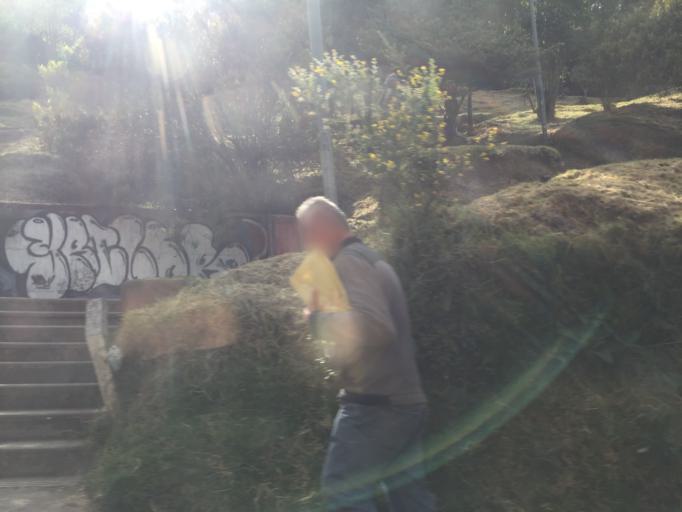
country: CO
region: Bogota D.C.
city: Bogota
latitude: 4.5996
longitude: -74.0655
